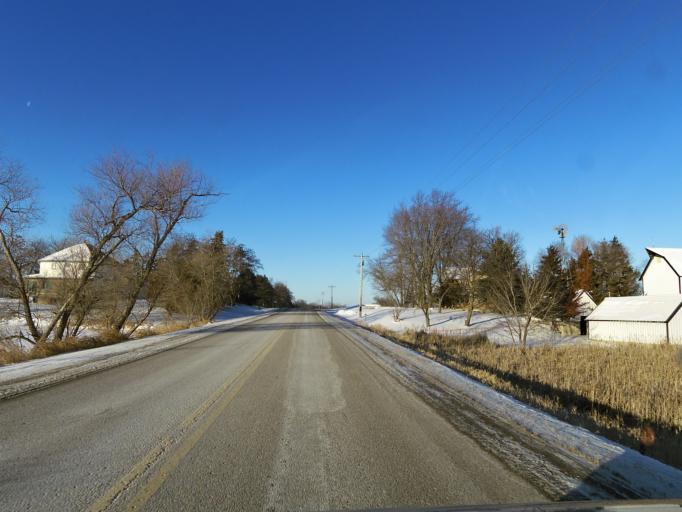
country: US
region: Minnesota
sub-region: Scott County
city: Jordan
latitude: 44.6600
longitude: -93.6042
